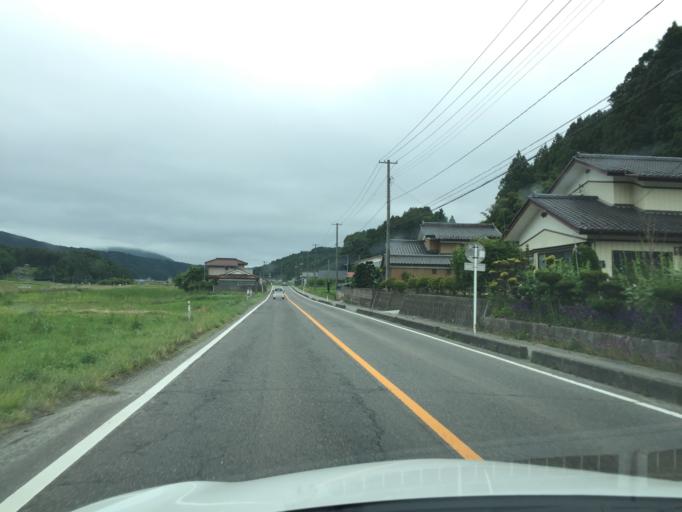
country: JP
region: Fukushima
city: Funehikimachi-funehiki
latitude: 37.3436
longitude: 140.6520
